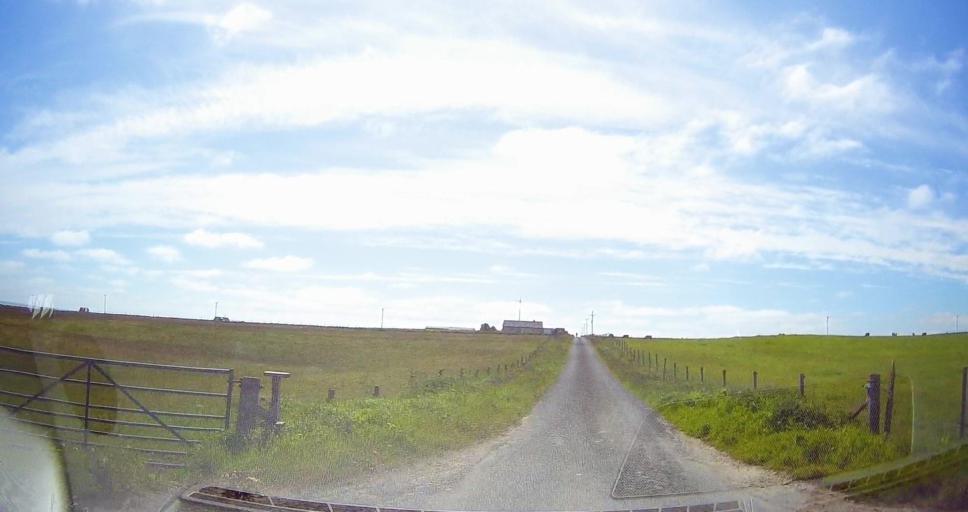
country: GB
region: Scotland
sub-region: Orkney Islands
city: Kirkwall
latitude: 58.8336
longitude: -2.9000
